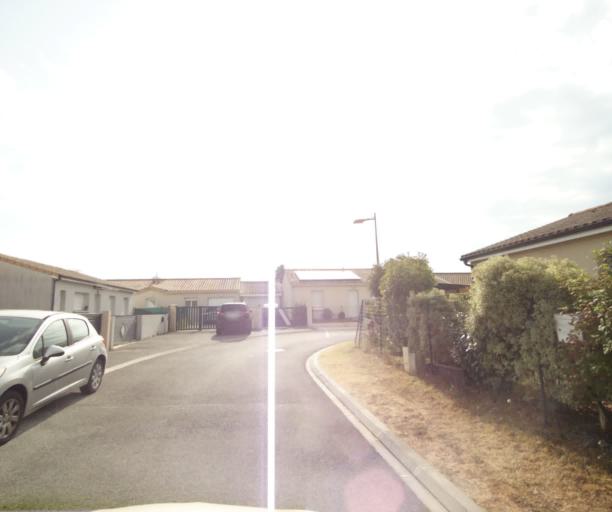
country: FR
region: Aquitaine
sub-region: Departement de la Gironde
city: Creon
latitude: 44.7699
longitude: -0.3492
